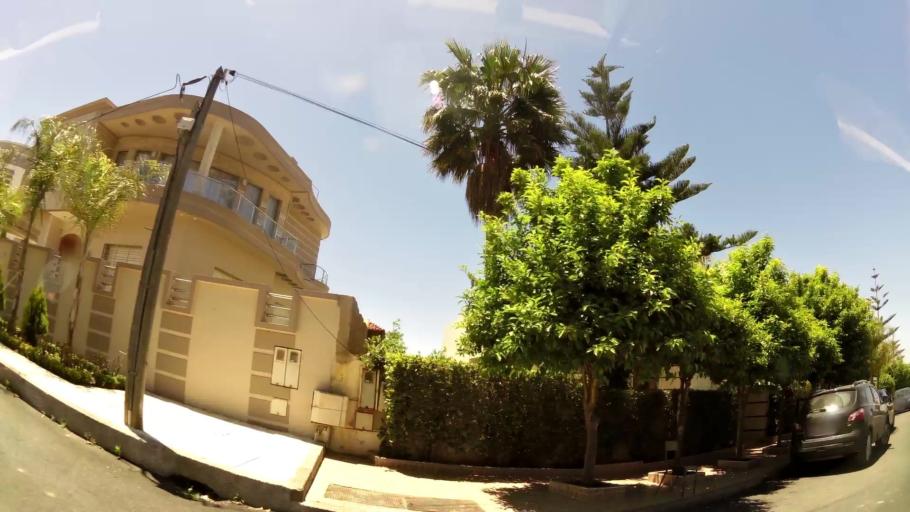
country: MA
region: Meknes-Tafilalet
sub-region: Meknes
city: Meknes
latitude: 33.9076
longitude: -5.5486
